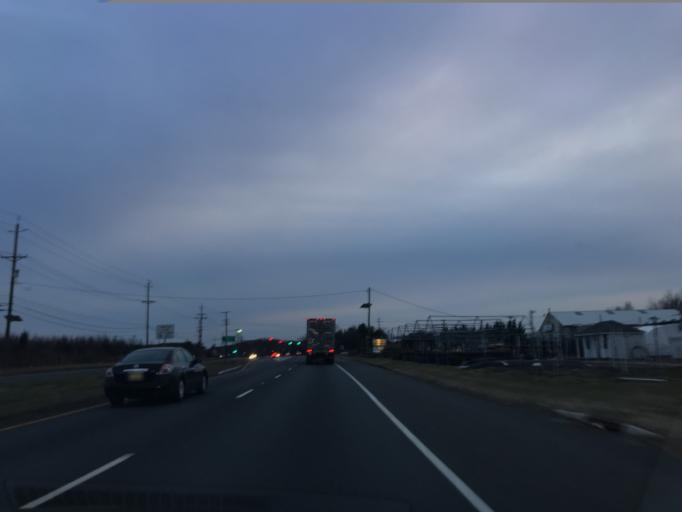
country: US
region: New Jersey
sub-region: Middlesex County
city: Dayton
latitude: 40.4036
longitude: -74.5084
